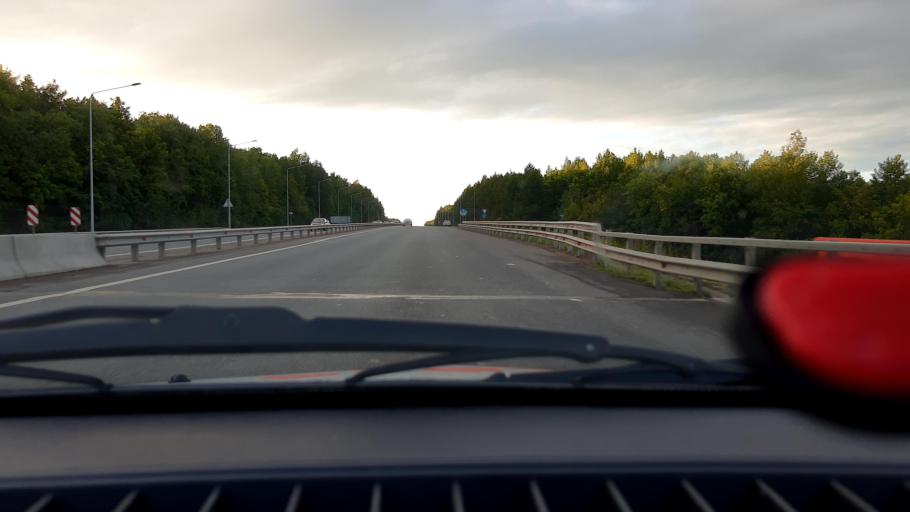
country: RU
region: Bashkortostan
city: Karmaskaly
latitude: 54.3798
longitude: 55.9173
